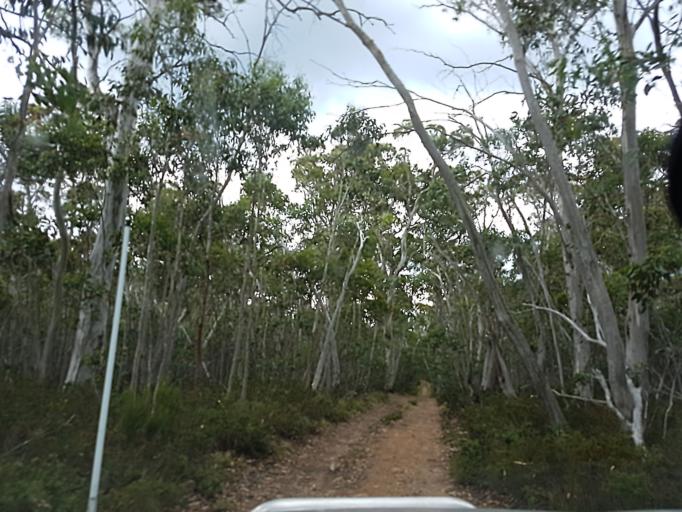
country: AU
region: New South Wales
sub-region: Snowy River
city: Jindabyne
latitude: -36.8777
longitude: 148.1606
